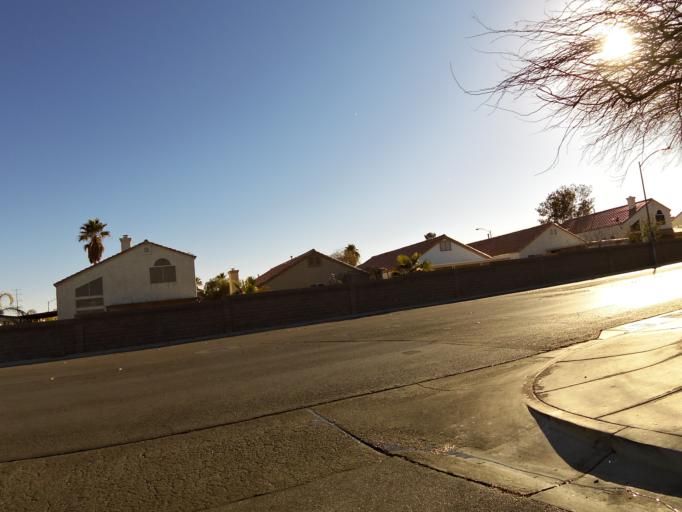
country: US
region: Nevada
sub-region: Clark County
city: Spring Valley
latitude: 36.1224
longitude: -115.2798
